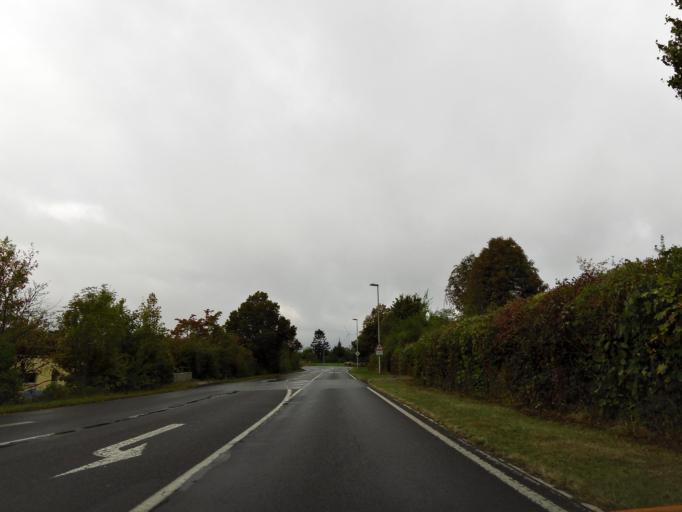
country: DE
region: Rheinland-Pfalz
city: Kastellaun
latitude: 50.0711
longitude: 7.4478
